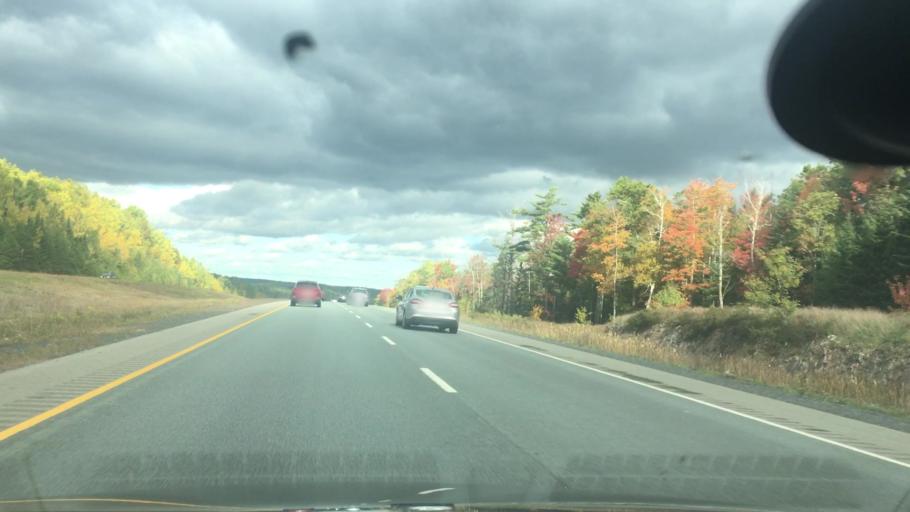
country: CA
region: Nova Scotia
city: Windsor
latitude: 44.9497
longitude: -64.0065
